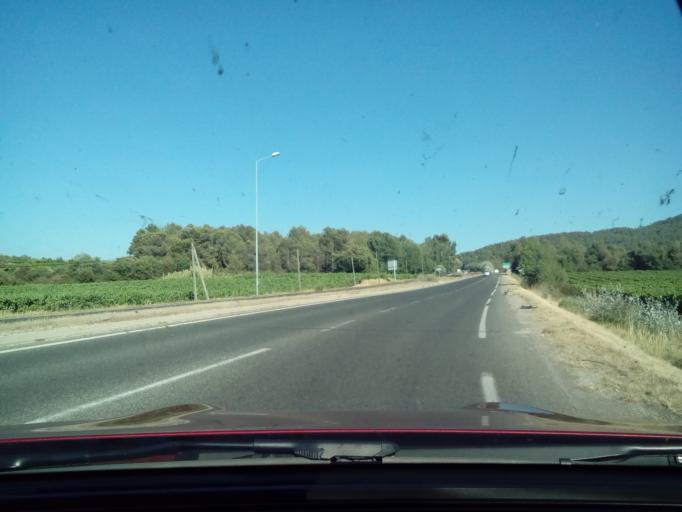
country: FR
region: Provence-Alpes-Cote d'Azur
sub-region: Departement du Var
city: Pourrieres
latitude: 43.4759
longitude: 5.7613
